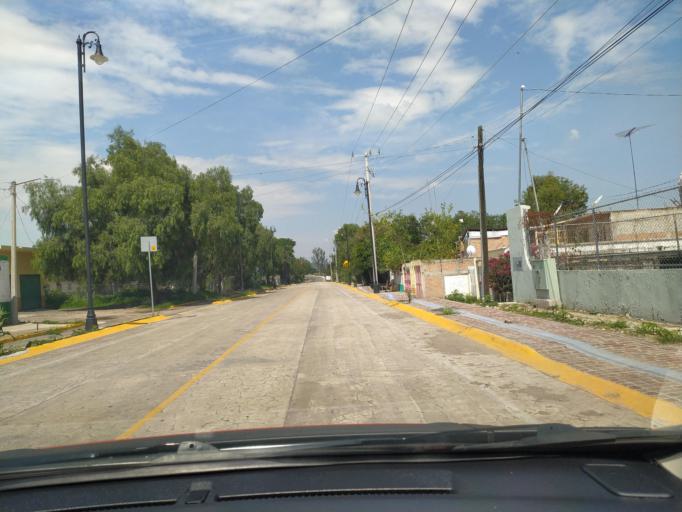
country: MX
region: Jalisco
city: San Diego de Alejandria
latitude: 20.8855
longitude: -101.9763
